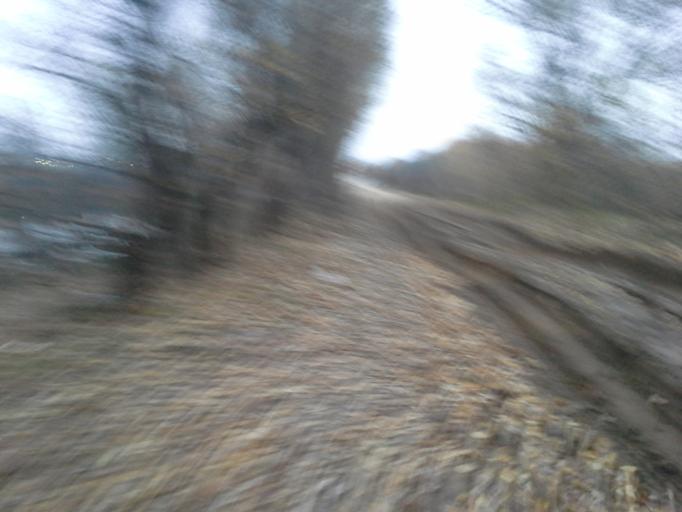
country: RU
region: Moskovskaya
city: Kommunarka
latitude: 55.5472
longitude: 37.4728
